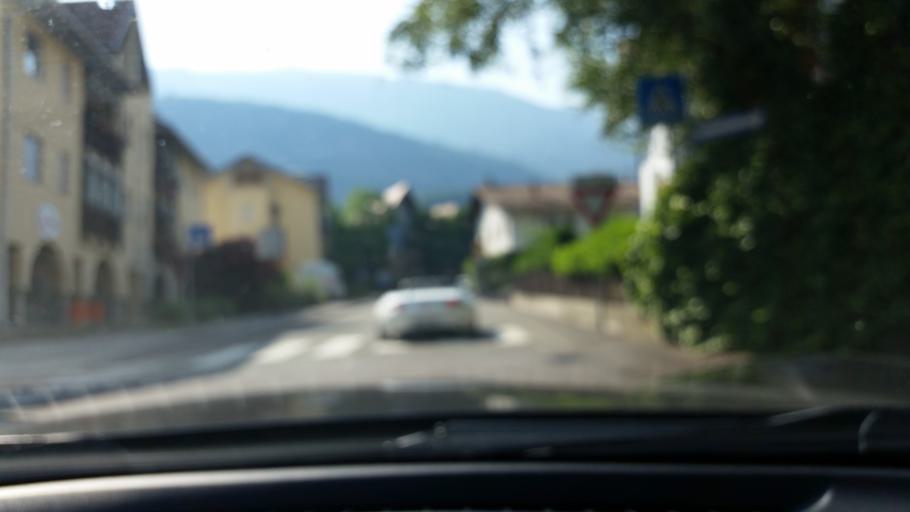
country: IT
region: Trentino-Alto Adige
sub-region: Bolzano
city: Ora
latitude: 46.3470
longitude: 11.2947
